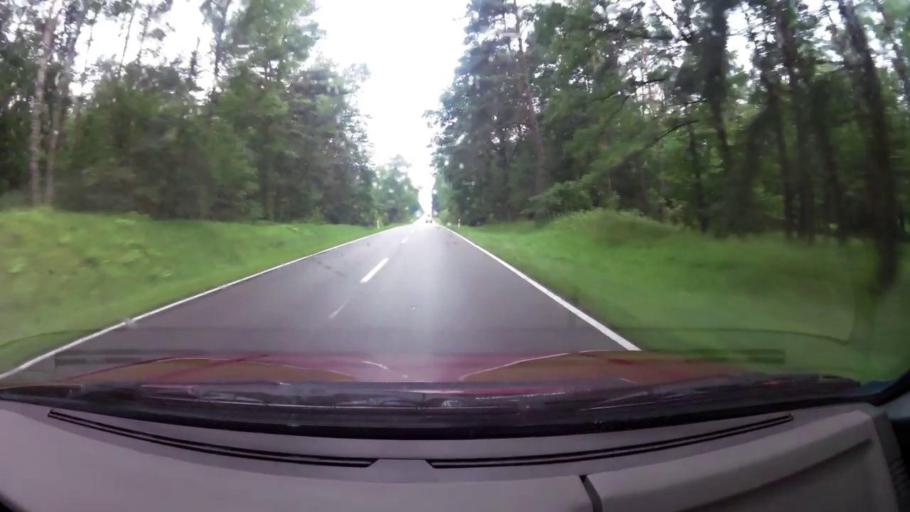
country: PL
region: West Pomeranian Voivodeship
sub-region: Powiat stargardzki
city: Marianowo
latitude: 53.3995
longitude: 15.2103
